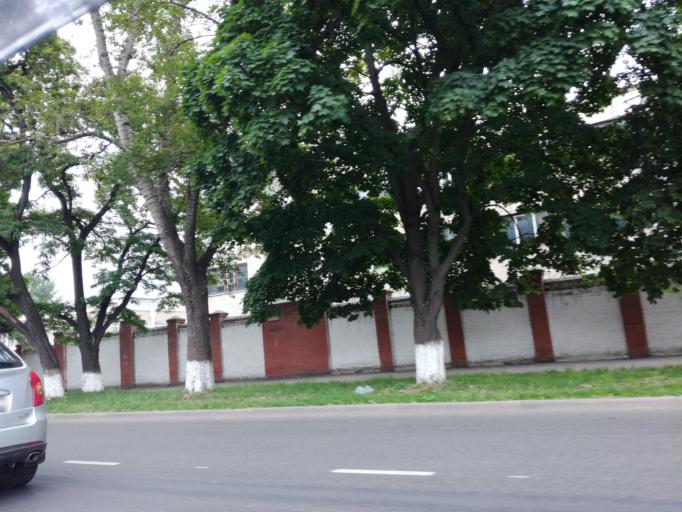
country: RU
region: Kursk
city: Kursk
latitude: 51.7244
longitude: 36.1626
